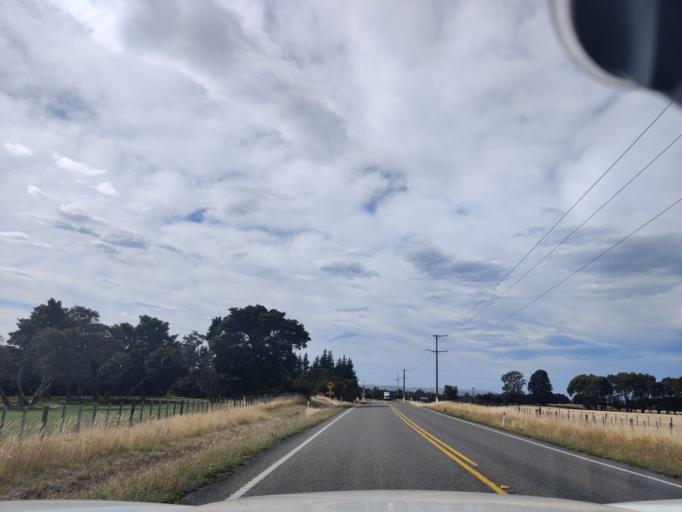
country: NZ
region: Wellington
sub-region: Masterton District
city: Masterton
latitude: -40.8405
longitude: 175.6308
